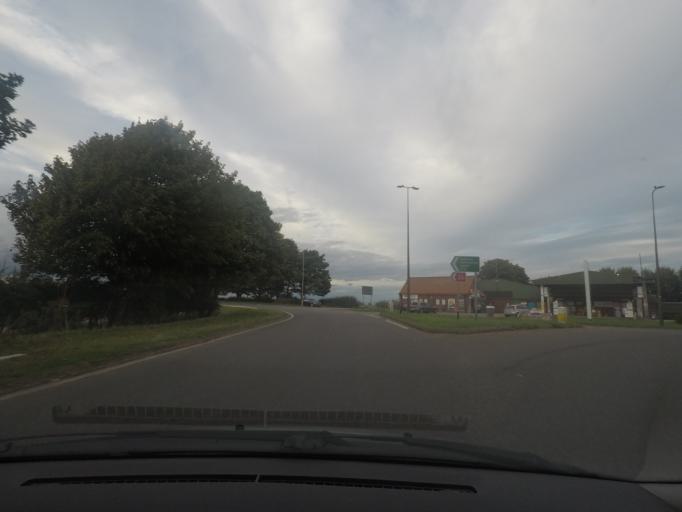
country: GB
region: England
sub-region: Lincolnshire
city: Alford
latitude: 53.2414
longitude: 0.1141
